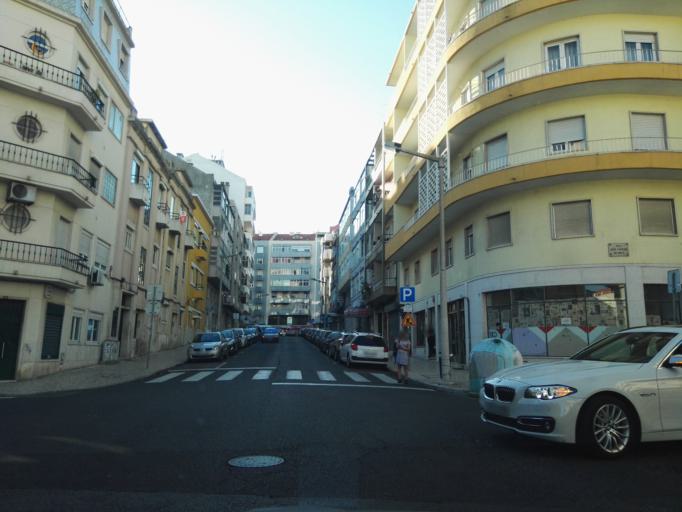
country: PT
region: Lisbon
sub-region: Lisbon
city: Lisbon
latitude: 38.7479
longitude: -9.1386
